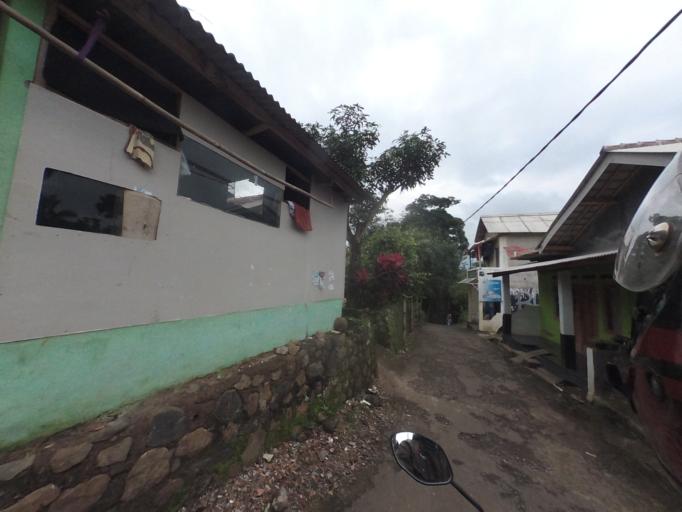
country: ID
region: West Java
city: Bogor
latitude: -6.6155
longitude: 106.7345
